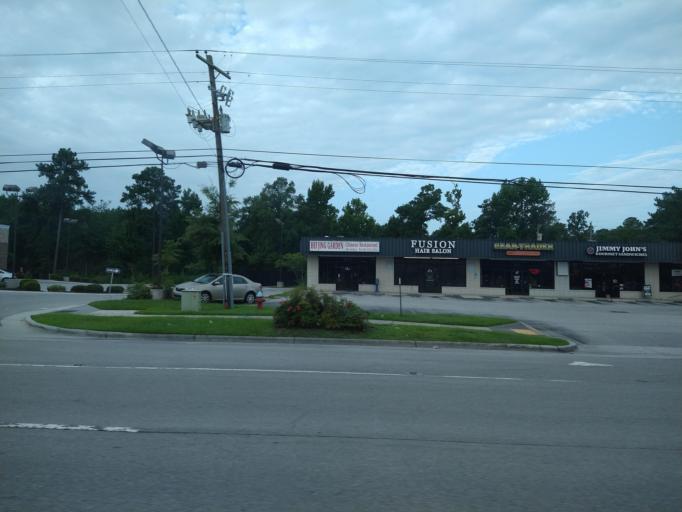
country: US
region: North Carolina
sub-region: Onslow County
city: Pumpkin Center
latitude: 34.7706
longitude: -77.3866
